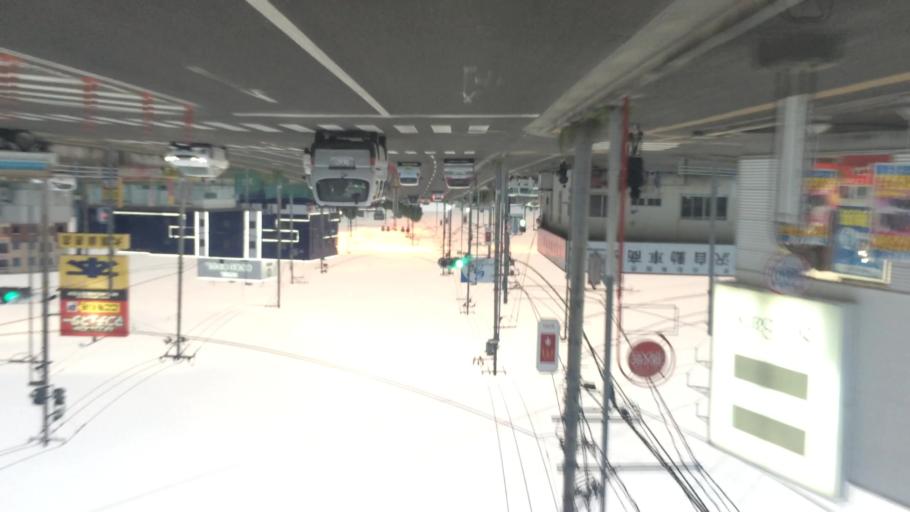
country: JP
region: Miyagi
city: Sendai-shi
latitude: 38.3159
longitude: 140.8989
